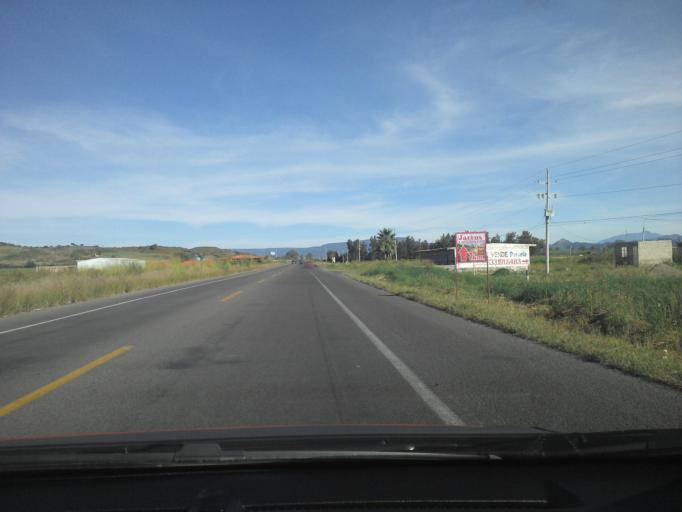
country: MX
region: Jalisco
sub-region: Teuchitlan
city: La Estanzuela
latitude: 20.6693
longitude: -103.8020
